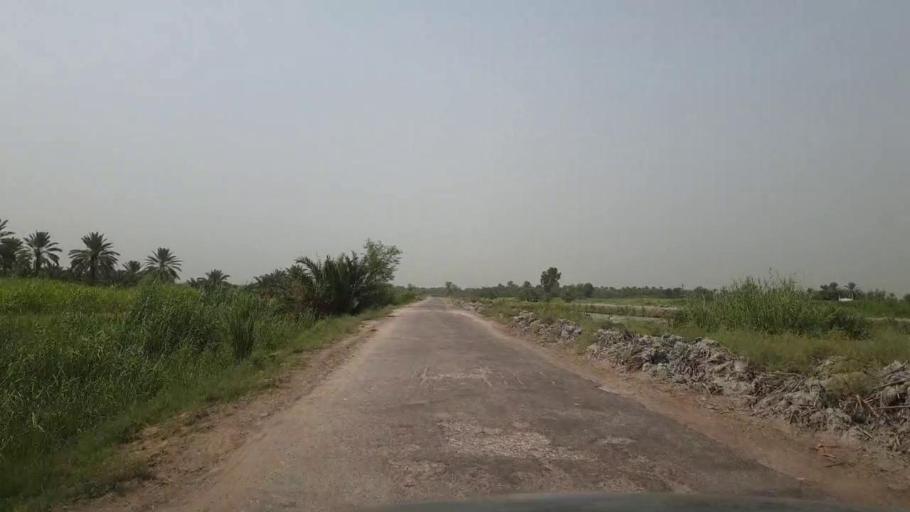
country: PK
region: Sindh
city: Gambat
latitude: 27.3895
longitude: 68.5497
